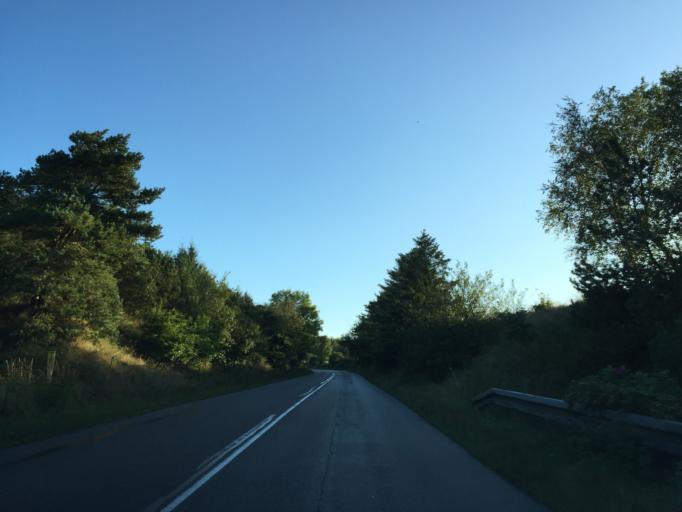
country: DK
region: Central Jutland
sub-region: Viborg Kommune
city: Bjerringbro
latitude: 56.3471
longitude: 9.6559
